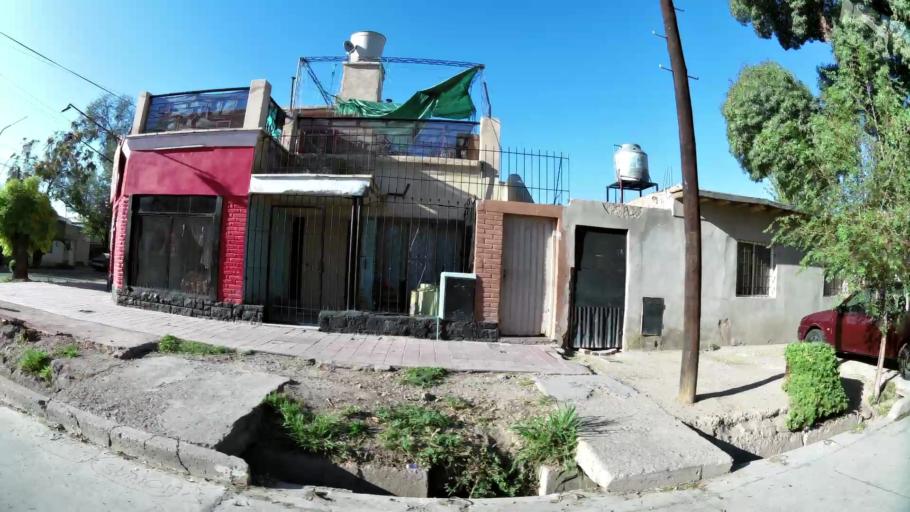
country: AR
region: Mendoza
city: Las Heras
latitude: -32.8539
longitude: -68.8315
